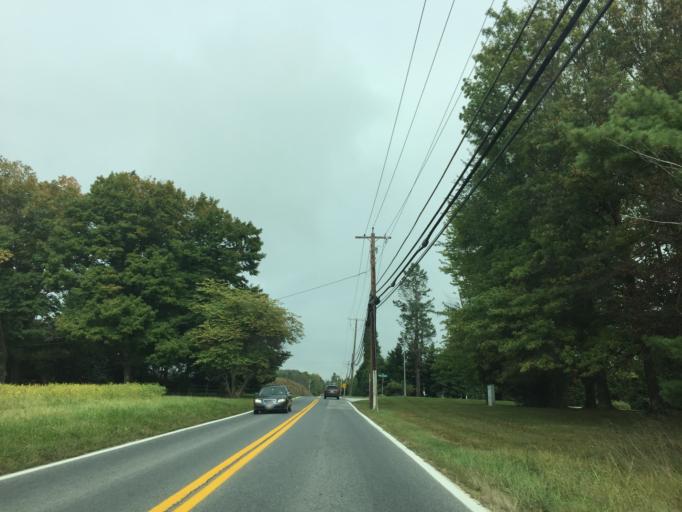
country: US
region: Maryland
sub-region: Baltimore County
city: Garrison
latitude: 39.4519
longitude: -76.7255
